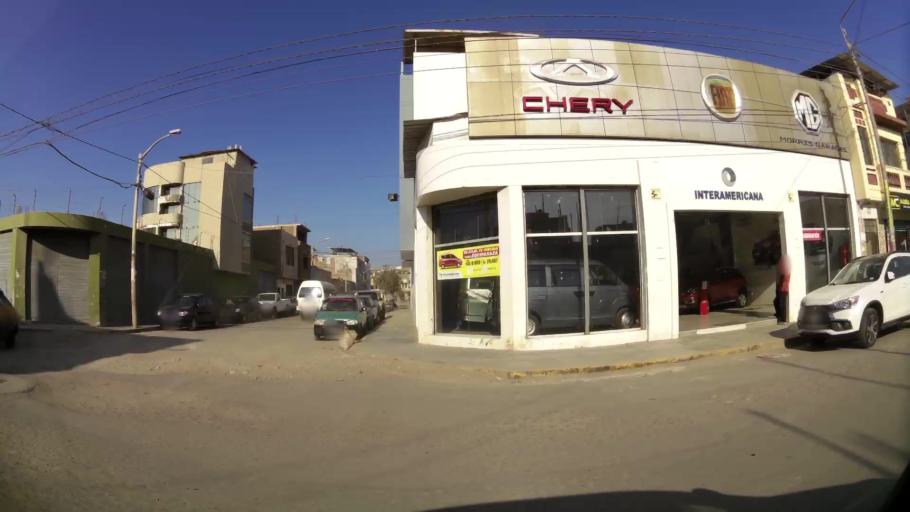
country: PE
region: Lambayeque
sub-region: Provincia de Chiclayo
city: Santa Rosa
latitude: -6.7664
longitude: -79.8350
